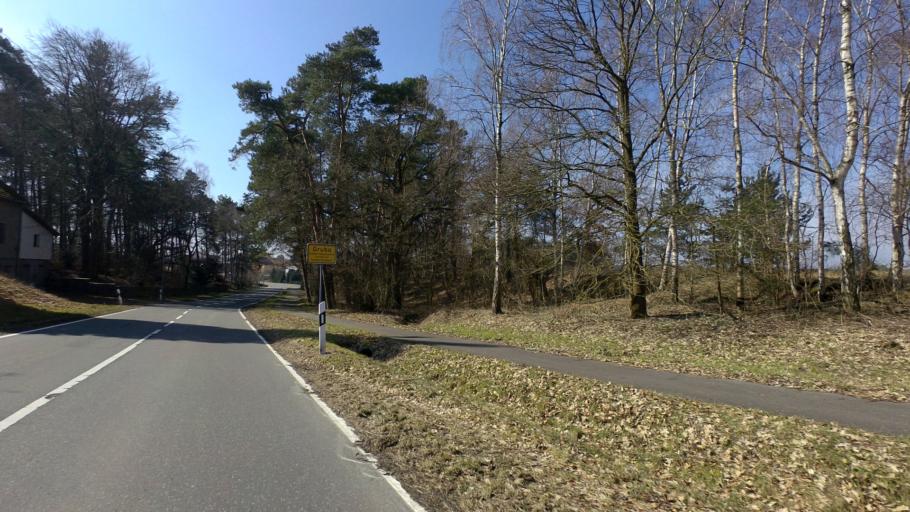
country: DE
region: Brandenburg
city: Wiesenburg
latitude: 52.0791
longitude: 12.5301
